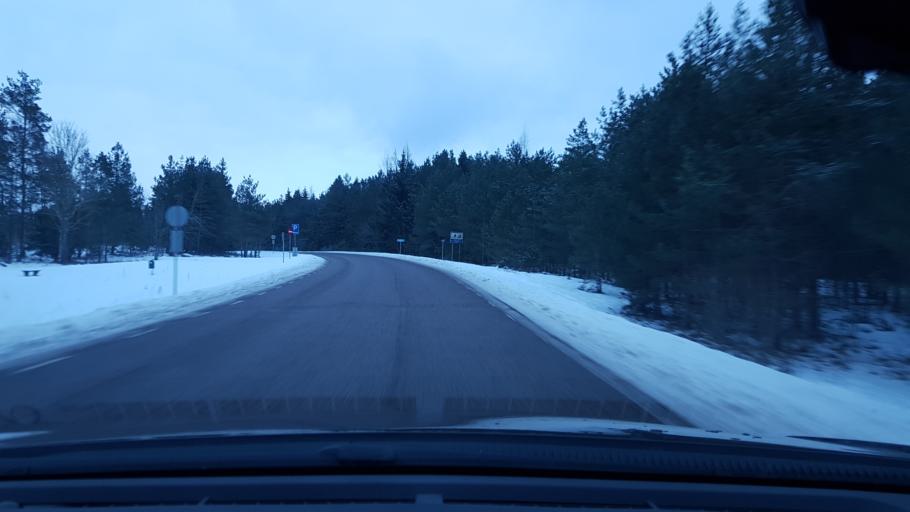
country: EE
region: Laeaene
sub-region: Ridala Parish
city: Uuemoisa
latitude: 59.0219
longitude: 23.6688
